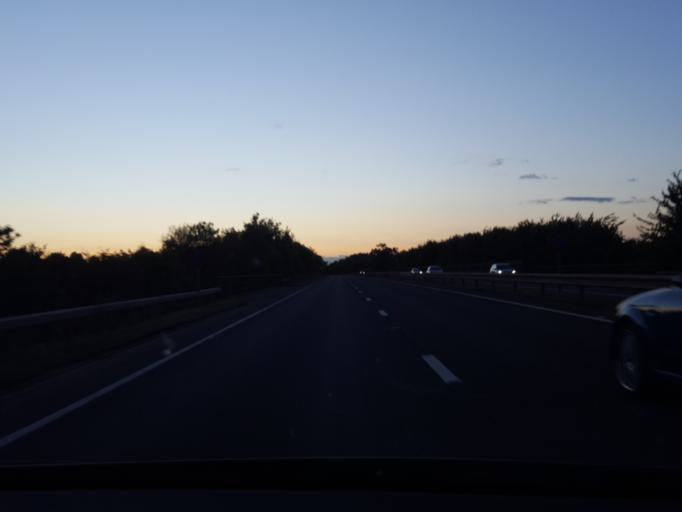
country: GB
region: England
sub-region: Leicestershire
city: Barrow upon Soar
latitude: 52.7460
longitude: -1.1545
